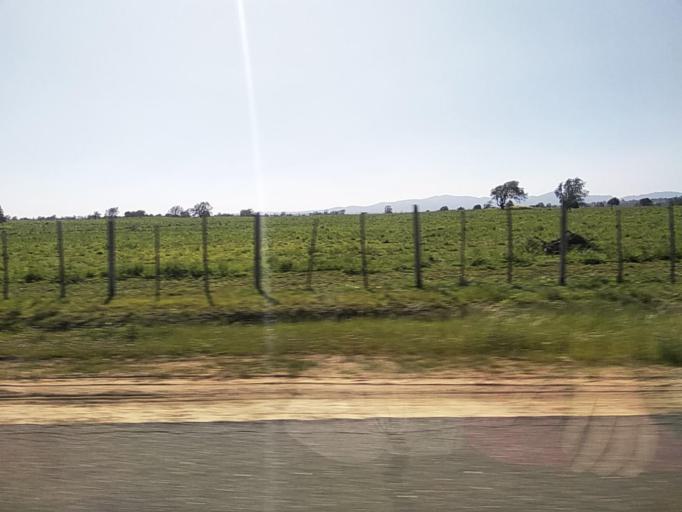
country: CL
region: Valparaiso
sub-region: San Antonio Province
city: El Tabo
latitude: -33.4065
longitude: -71.5341
